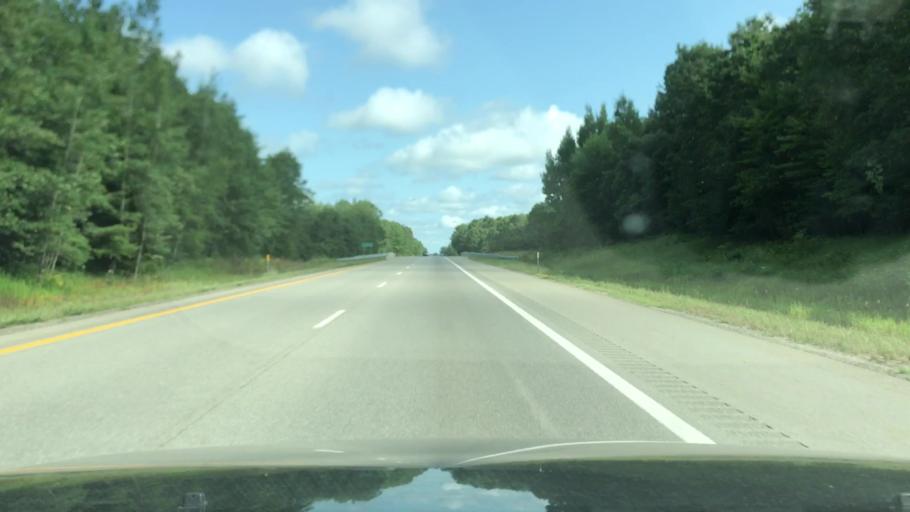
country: US
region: Michigan
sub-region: Montcalm County
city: Howard City
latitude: 43.5097
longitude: -85.4860
